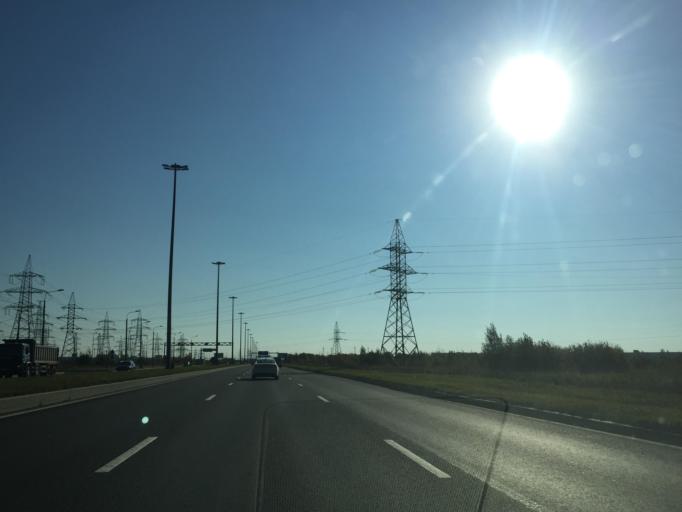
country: RU
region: St.-Petersburg
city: Petro-Slavyanka
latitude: 59.7548
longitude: 30.5209
